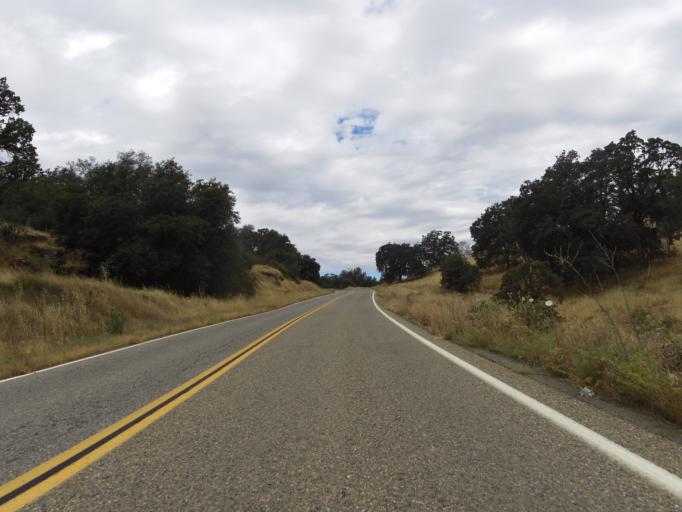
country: US
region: California
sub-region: Madera County
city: Yosemite Lakes
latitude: 37.2396
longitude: -119.7924
